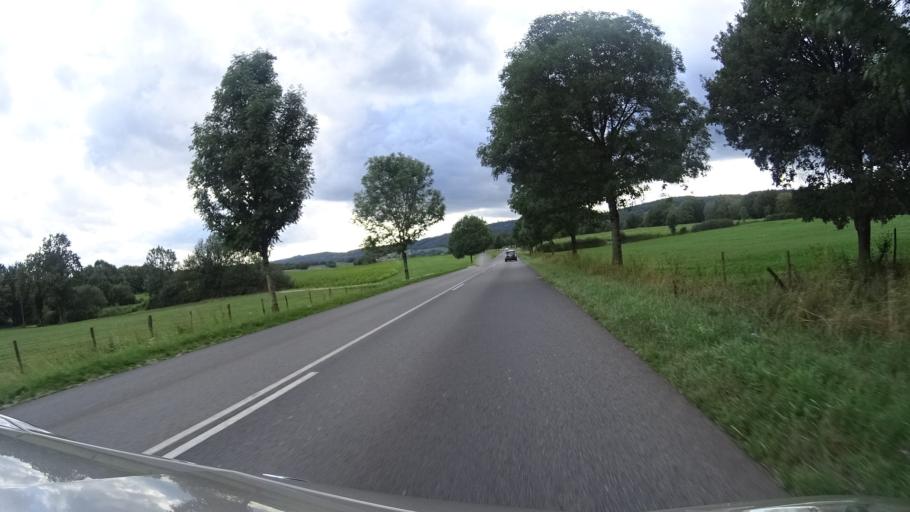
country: FR
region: Franche-Comte
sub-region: Departement du Doubs
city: Saone
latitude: 47.2429
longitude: 6.1408
